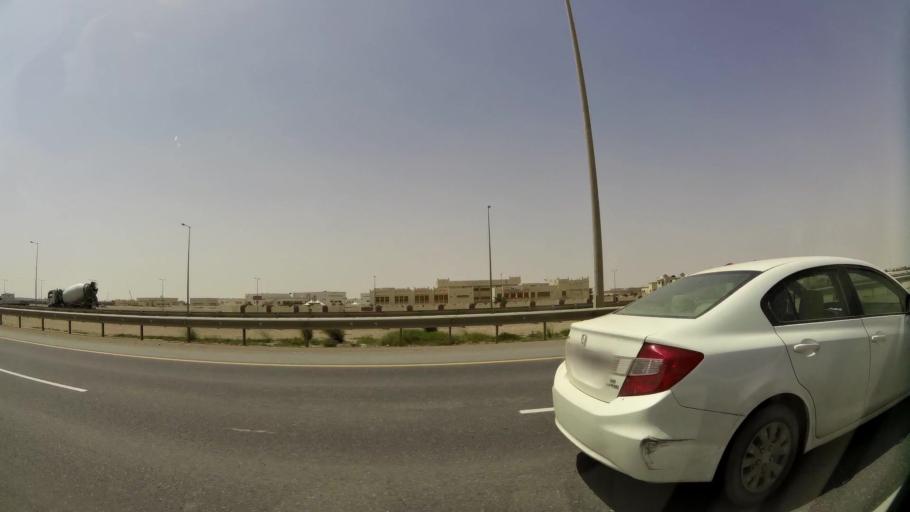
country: QA
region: Baladiyat Umm Salal
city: Umm Salal Muhammad
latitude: 25.4219
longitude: 51.4192
